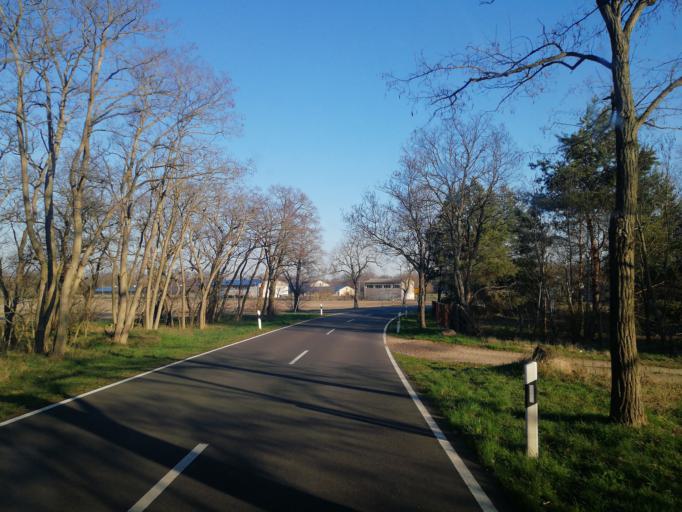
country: DE
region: Brandenburg
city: Drahnsdorf
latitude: 51.9135
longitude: 13.5943
